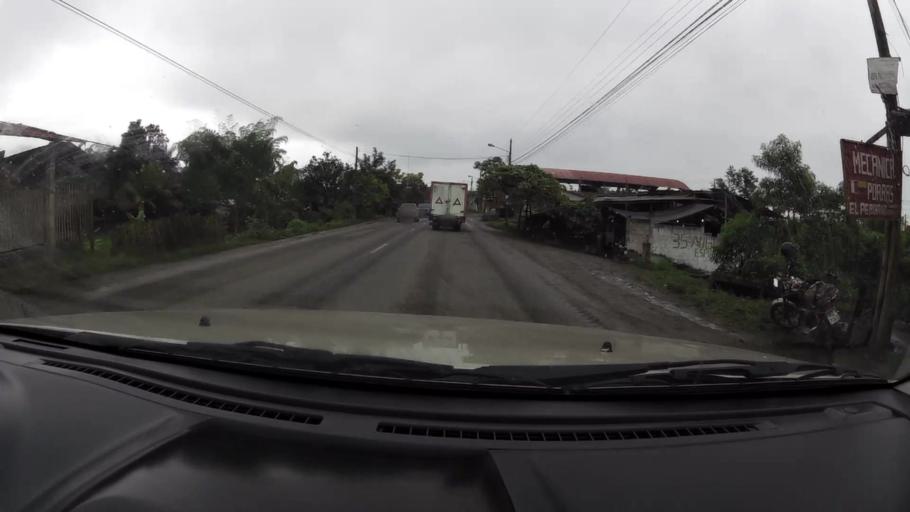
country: EC
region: Guayas
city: Balao
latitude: -3.0522
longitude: -79.7438
